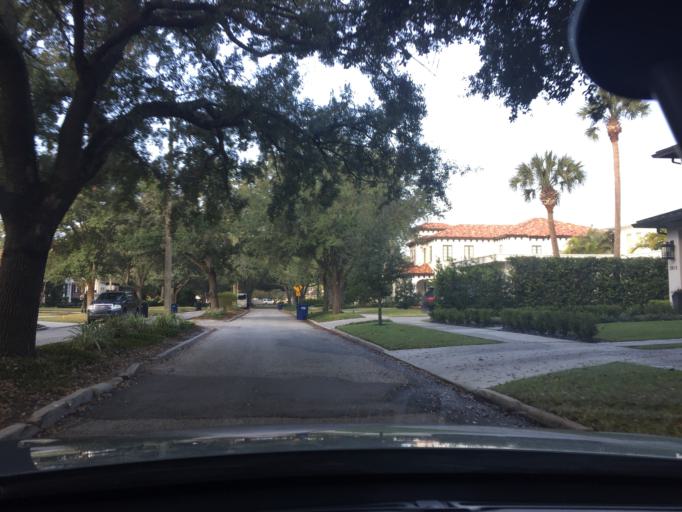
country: US
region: Florida
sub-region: Hillsborough County
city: Tampa
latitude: 27.9349
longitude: -82.4904
